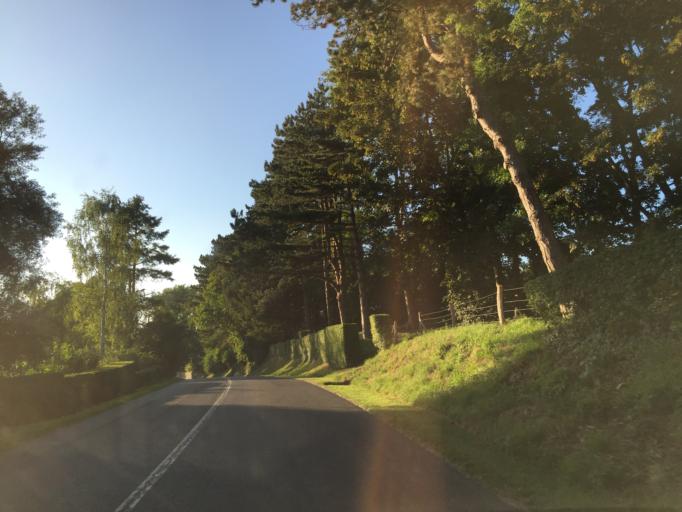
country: FR
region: Lower Normandy
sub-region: Departement du Calvados
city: Equemauville
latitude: 49.4048
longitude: 0.1788
